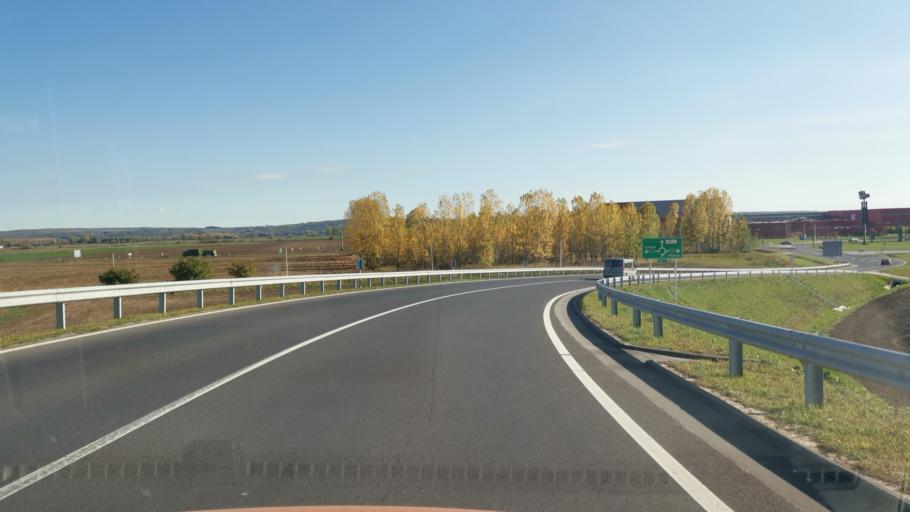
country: HU
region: Borsod-Abauj-Zemplen
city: Szikszo
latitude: 48.1788
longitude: 20.9120
